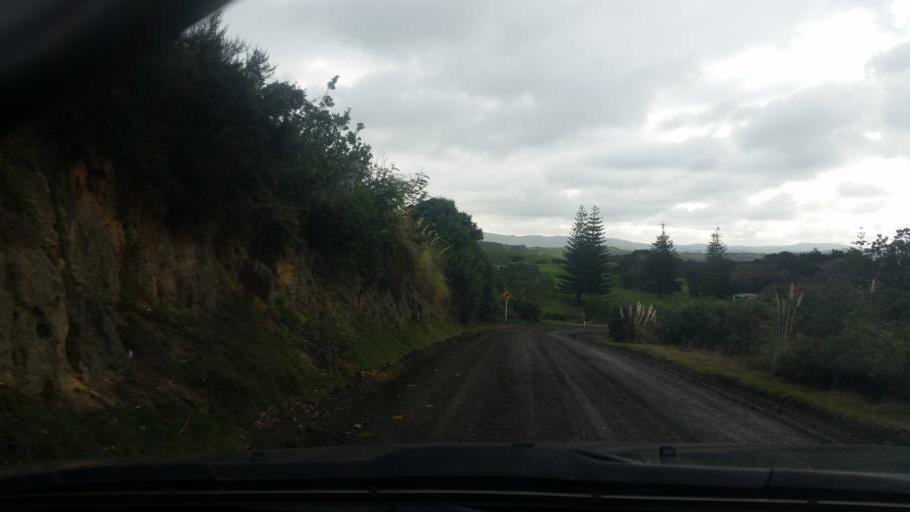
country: NZ
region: Northland
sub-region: Kaipara District
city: Dargaville
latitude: -35.8457
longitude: 173.6609
